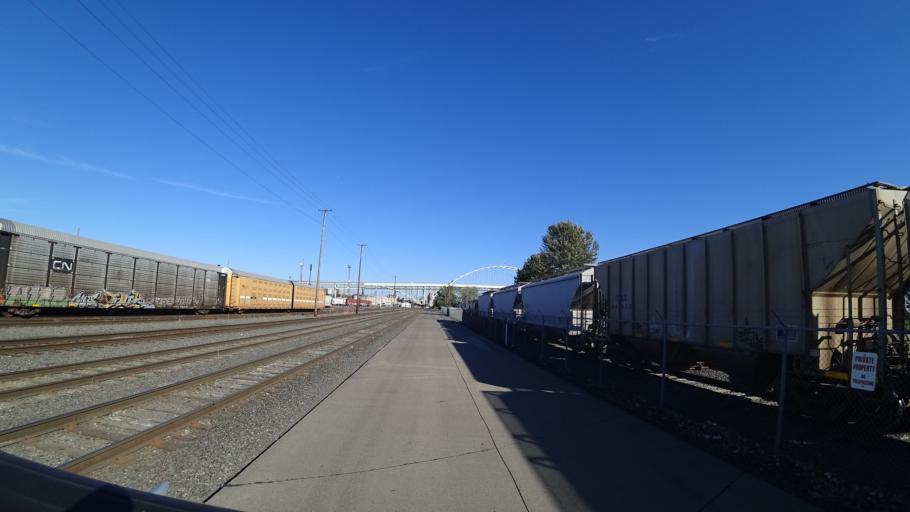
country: US
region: Oregon
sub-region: Multnomah County
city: Portland
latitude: 45.5450
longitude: -122.6883
